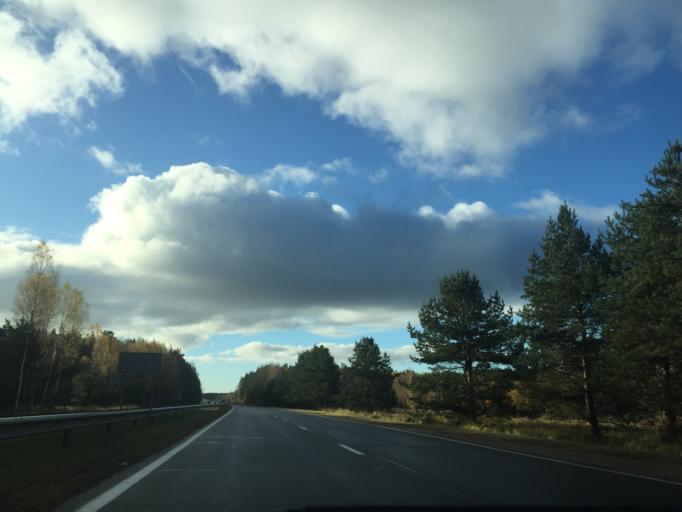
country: LV
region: Babite
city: Pinki
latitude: 56.9411
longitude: 23.9205
